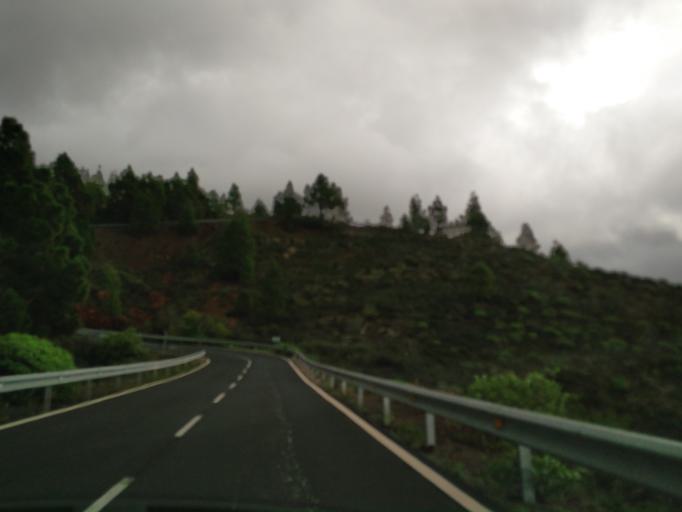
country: ES
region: Canary Islands
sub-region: Provincia de Santa Cruz de Tenerife
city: Arona
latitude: 28.1171
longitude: -16.6774
